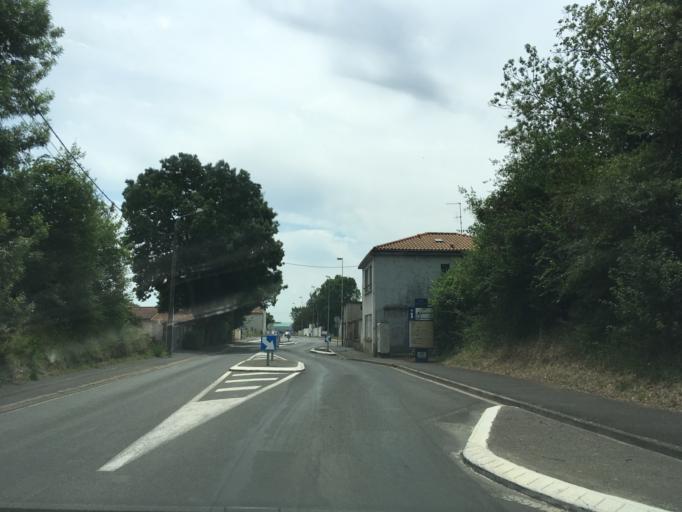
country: FR
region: Poitou-Charentes
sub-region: Departement des Deux-Sevres
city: Niort
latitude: 46.3084
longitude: -0.4608
